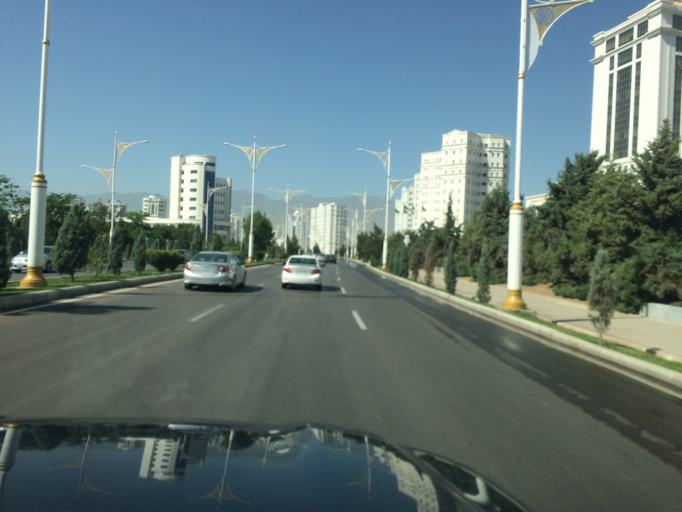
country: TM
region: Ahal
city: Ashgabat
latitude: 37.9136
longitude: 58.3697
